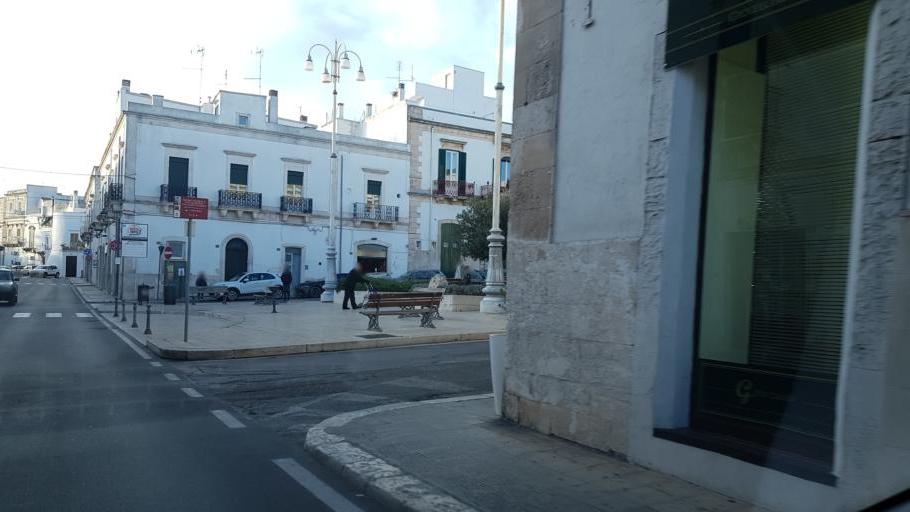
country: IT
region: Apulia
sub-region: Provincia di Taranto
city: Martina Franca
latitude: 40.7029
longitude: 17.3393
